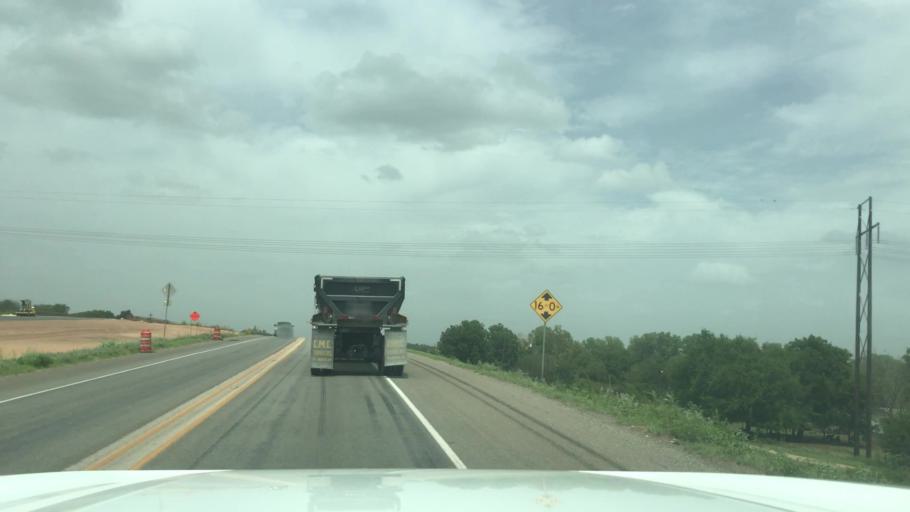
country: US
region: Texas
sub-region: McLennan County
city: Bellmead
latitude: 31.5416
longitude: -97.0702
